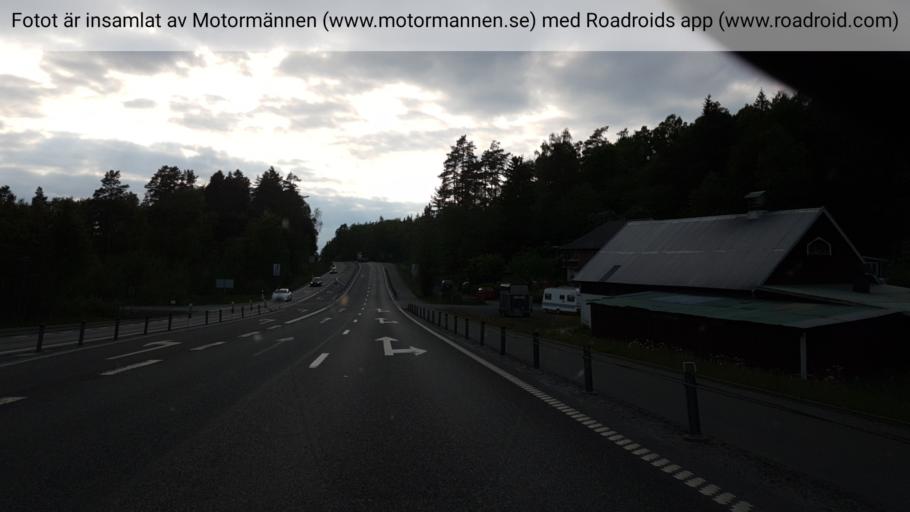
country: SE
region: Joenkoeping
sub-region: Jonkopings Kommun
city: Huskvarna
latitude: 57.7573
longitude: 14.2525
